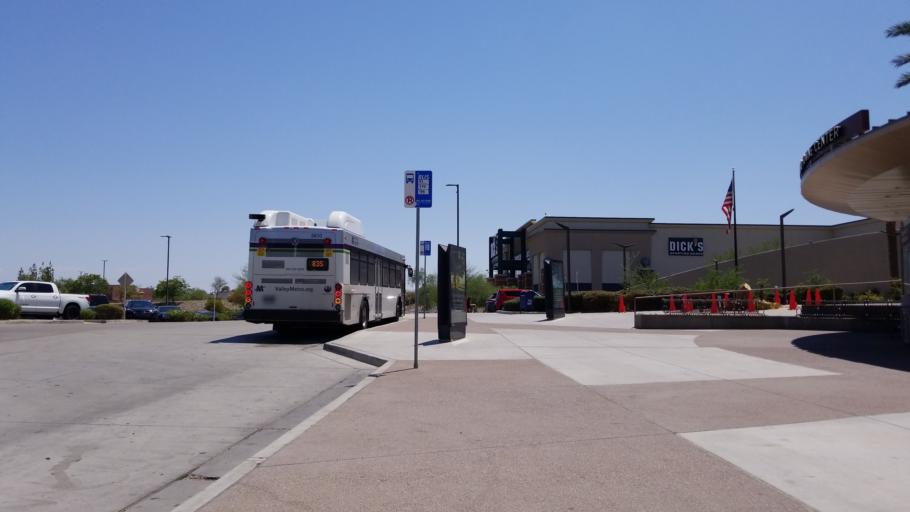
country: US
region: Arizona
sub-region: Maricopa County
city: Peoria
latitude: 33.6432
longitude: -112.2254
